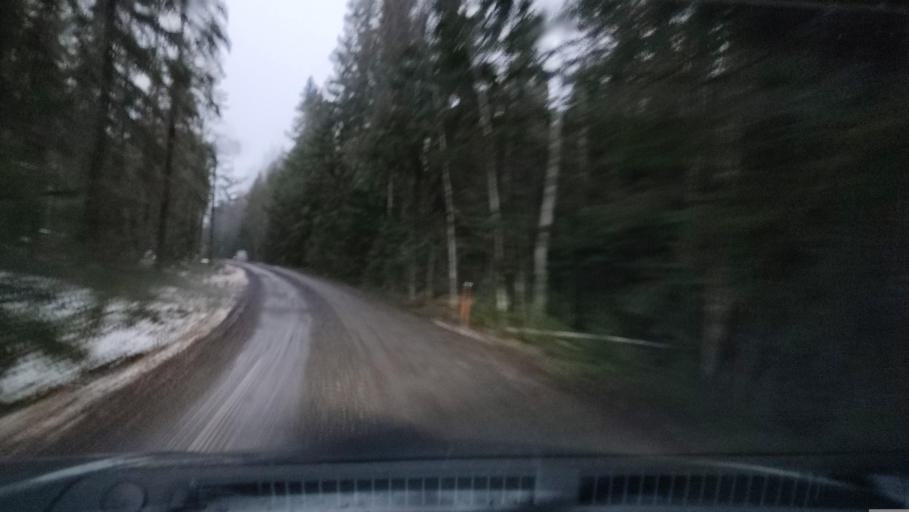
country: FI
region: Southern Ostrobothnia
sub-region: Suupohja
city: Karijoki
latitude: 62.1393
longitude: 21.6274
